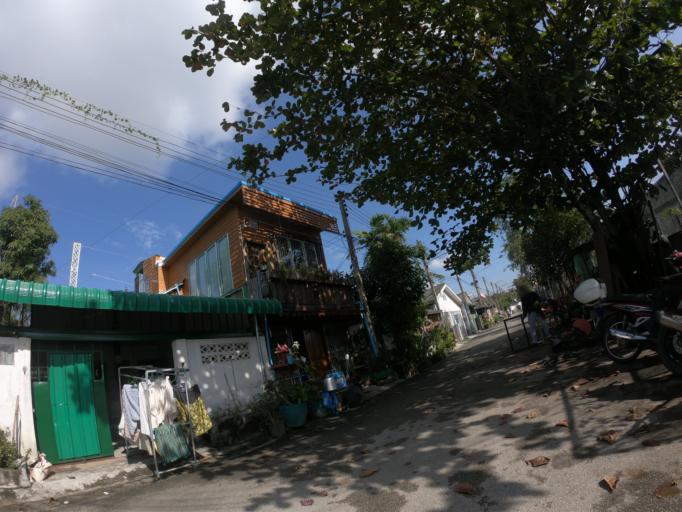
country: TH
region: Chiang Mai
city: Chiang Mai
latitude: 18.7867
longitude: 99.0379
